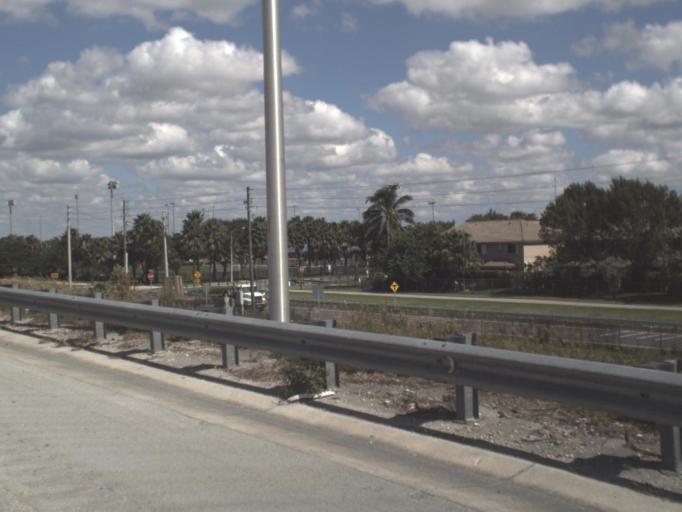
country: US
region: Florida
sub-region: Miami-Dade County
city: Doral
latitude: 25.8249
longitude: -80.3866
